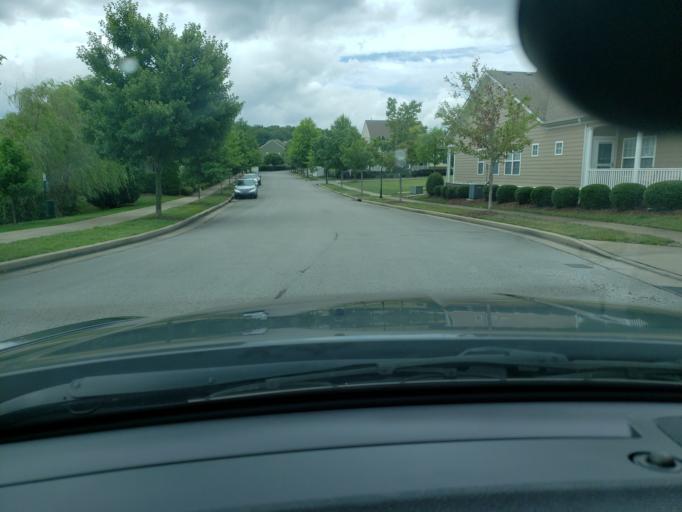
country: US
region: Tennessee
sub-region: Williamson County
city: Nolensville
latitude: 36.0188
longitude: -86.7011
